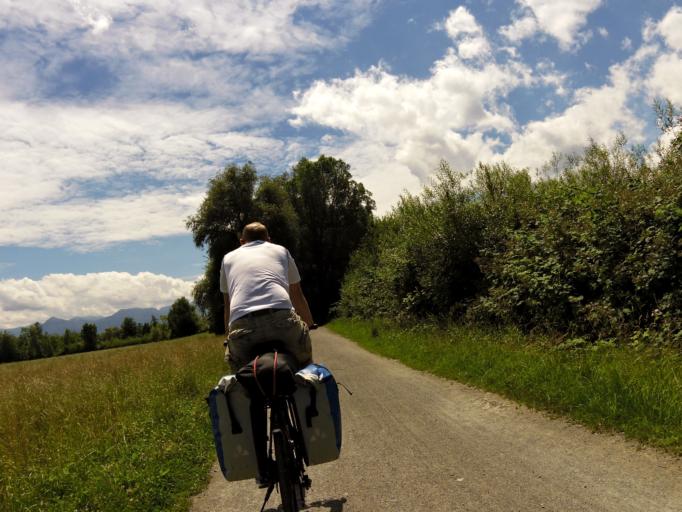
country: AT
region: Vorarlberg
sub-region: Politischer Bezirk Bregenz
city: Hard
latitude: 47.4948
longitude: 9.6759
